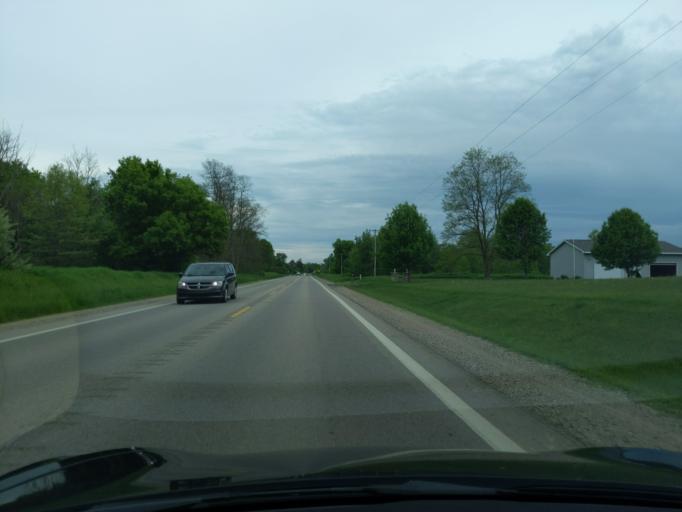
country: US
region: Michigan
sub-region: Jackson County
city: Michigan Center
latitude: 42.3570
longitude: -84.3293
